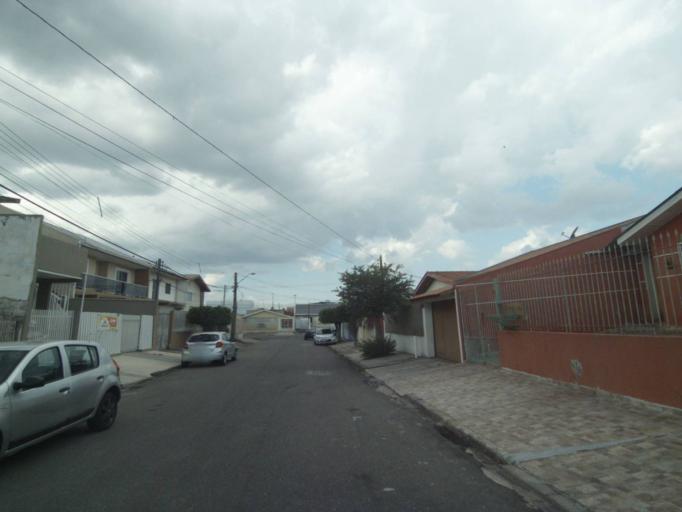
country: BR
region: Parana
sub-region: Sao Jose Dos Pinhais
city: Sao Jose dos Pinhais
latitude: -25.5302
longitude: -49.2630
